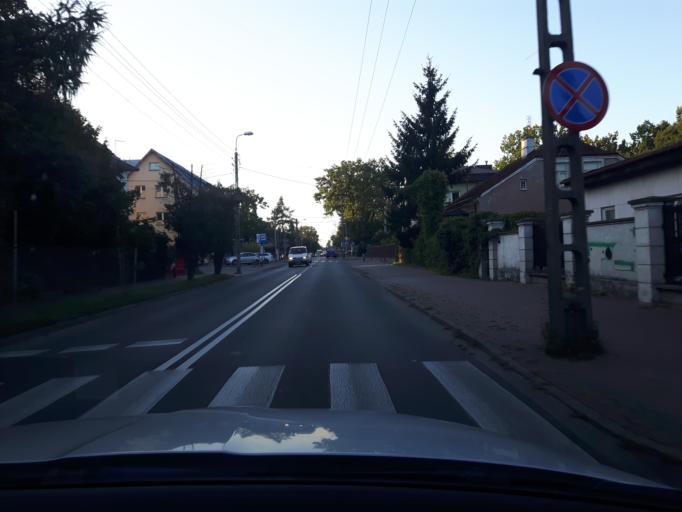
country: PL
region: Masovian Voivodeship
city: Zielonka
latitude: 52.3057
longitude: 21.1582
